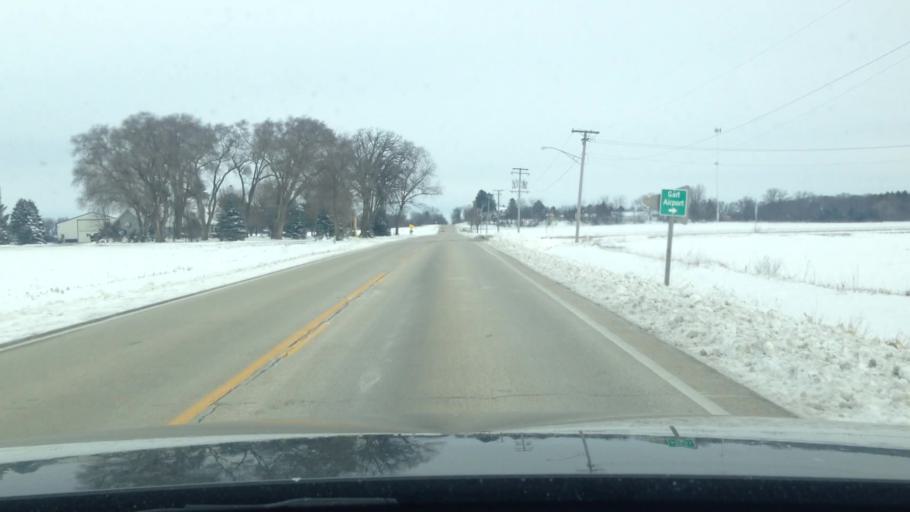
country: US
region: Illinois
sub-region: McHenry County
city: Hebron
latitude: 42.3987
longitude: -88.4382
